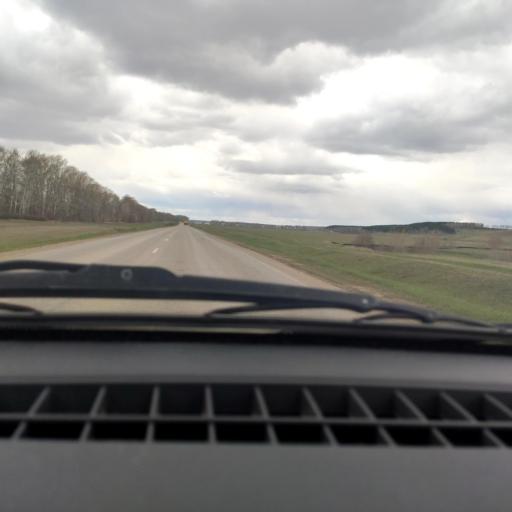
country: RU
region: Bashkortostan
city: Chekmagush
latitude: 55.1239
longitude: 54.7184
